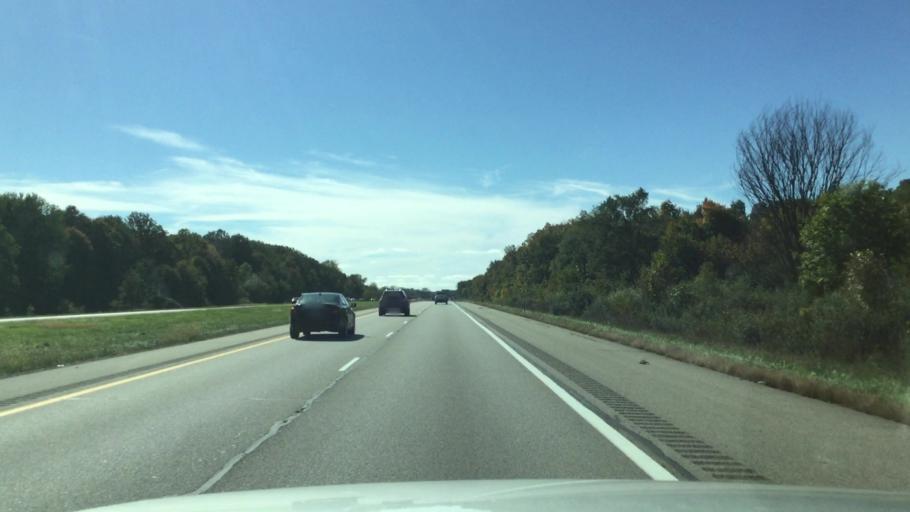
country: US
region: Michigan
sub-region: Washtenaw County
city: Ypsilanti
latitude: 42.3359
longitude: -83.6128
